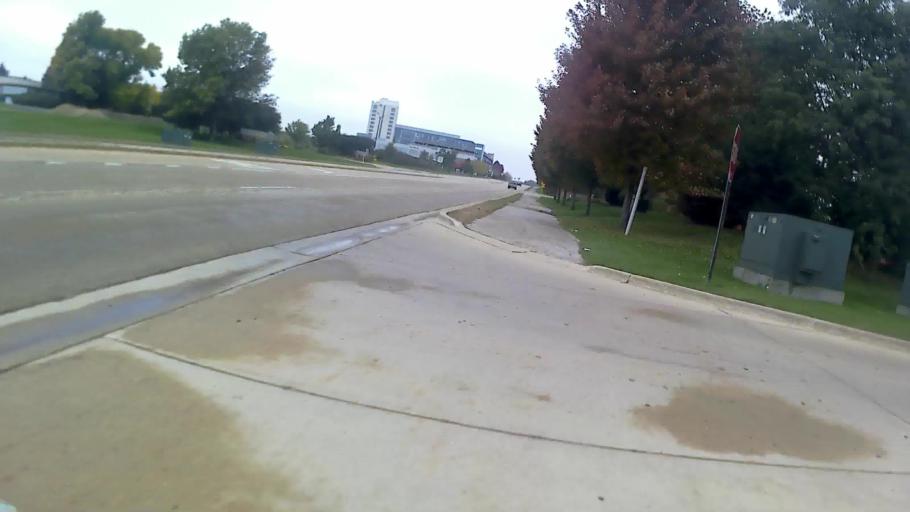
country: US
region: Illinois
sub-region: DuPage County
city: Warrenville
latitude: 41.8086
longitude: -88.1966
